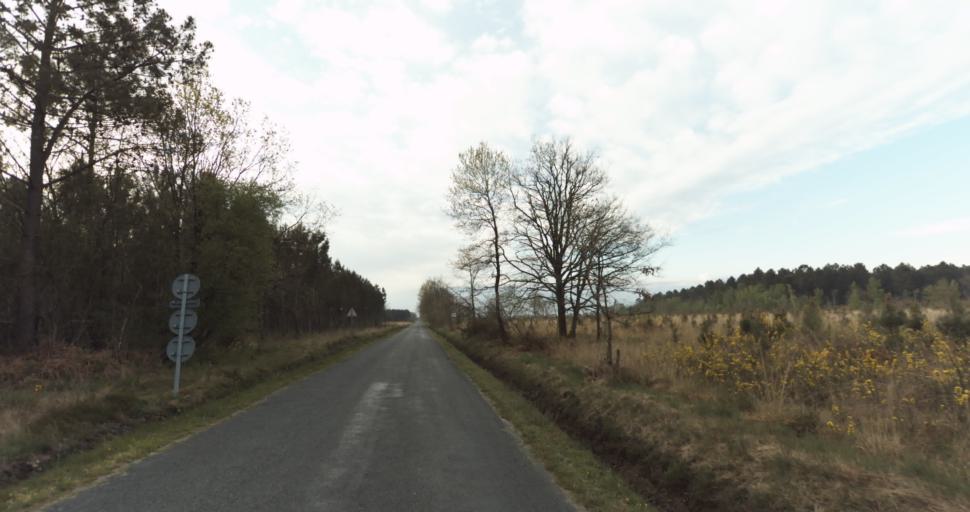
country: FR
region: Aquitaine
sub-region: Departement de la Gironde
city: Saint-Aubin-de-Medoc
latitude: 44.7893
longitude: -0.7560
